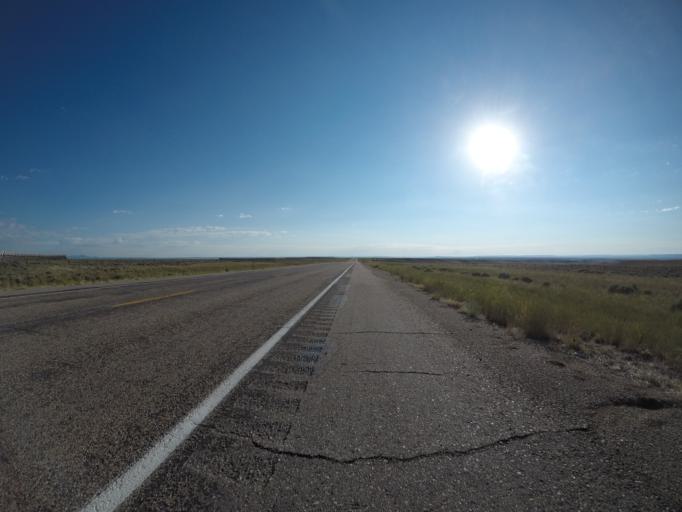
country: US
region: Wyoming
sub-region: Lincoln County
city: Kemmerer
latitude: 41.8979
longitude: -110.3320
